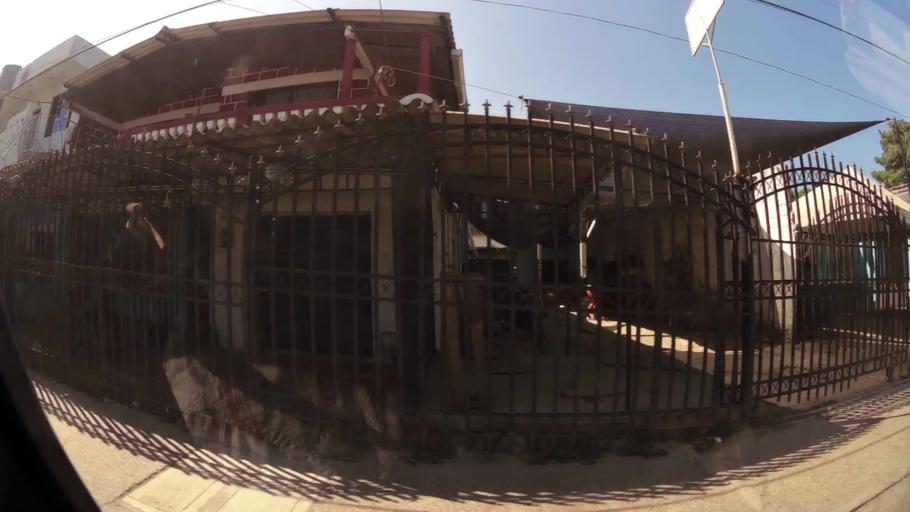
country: CO
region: Bolivar
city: Cartagena
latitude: 10.4158
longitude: -75.5199
